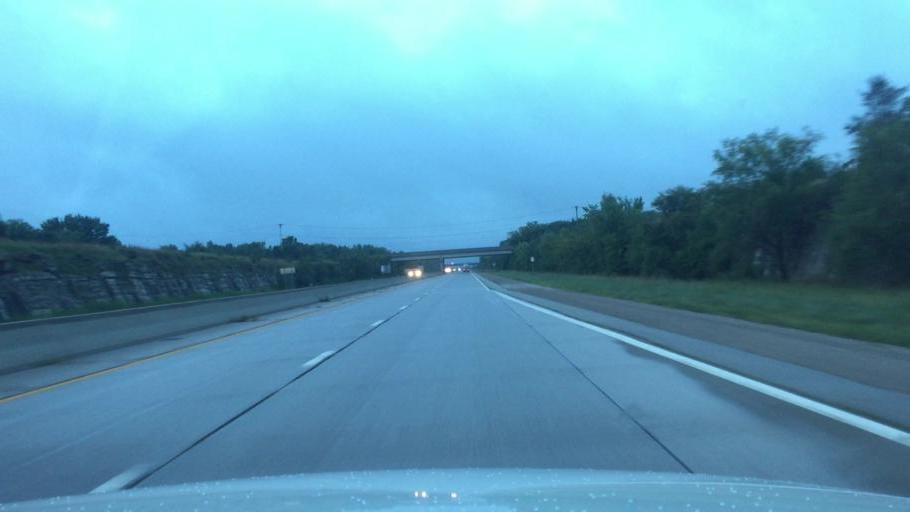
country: US
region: Kansas
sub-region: Neosho County
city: Chanute
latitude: 37.6847
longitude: -95.4796
